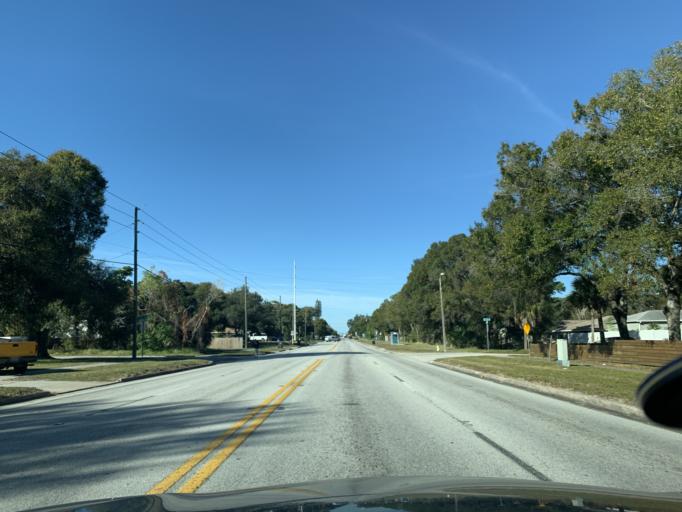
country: US
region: Florida
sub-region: Pinellas County
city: Lealman
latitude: 27.8284
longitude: -82.6694
